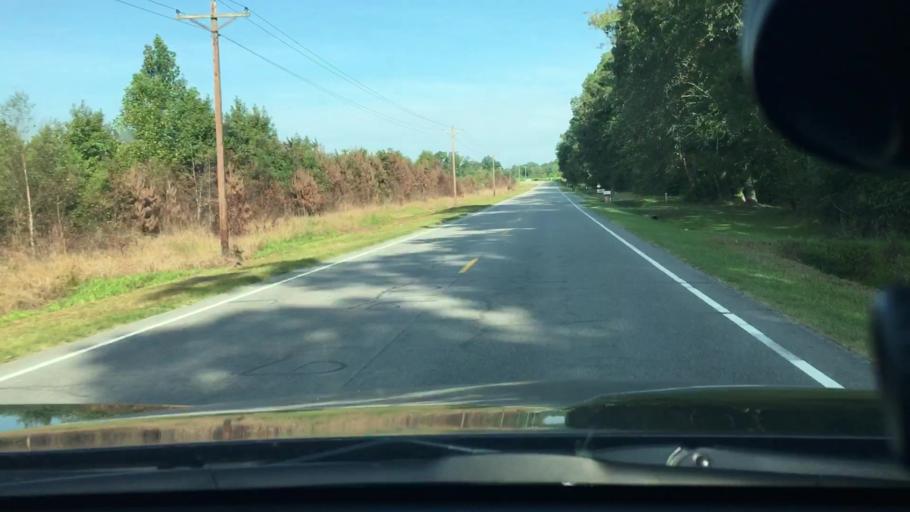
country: US
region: North Carolina
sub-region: Edgecombe County
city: Pinetops
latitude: 35.7861
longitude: -77.6213
